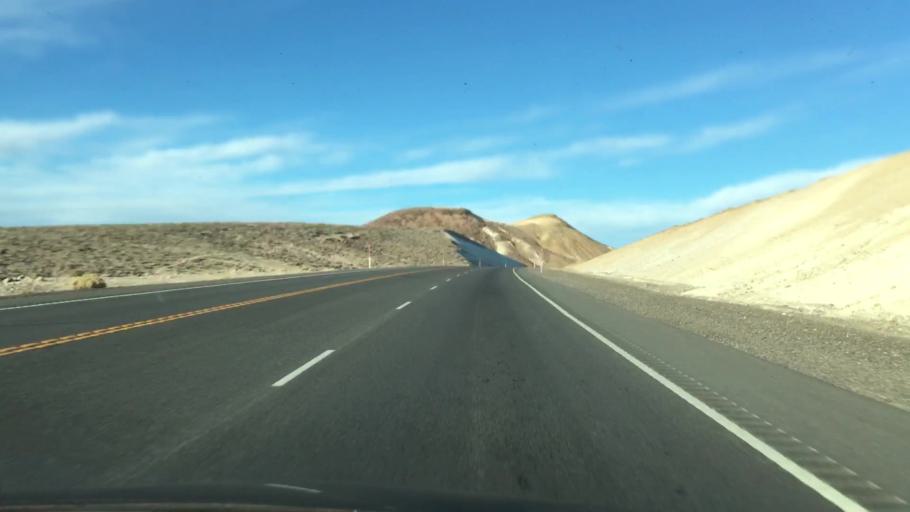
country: US
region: Nevada
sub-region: Nye County
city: Tonopah
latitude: 37.9913
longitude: -117.2729
